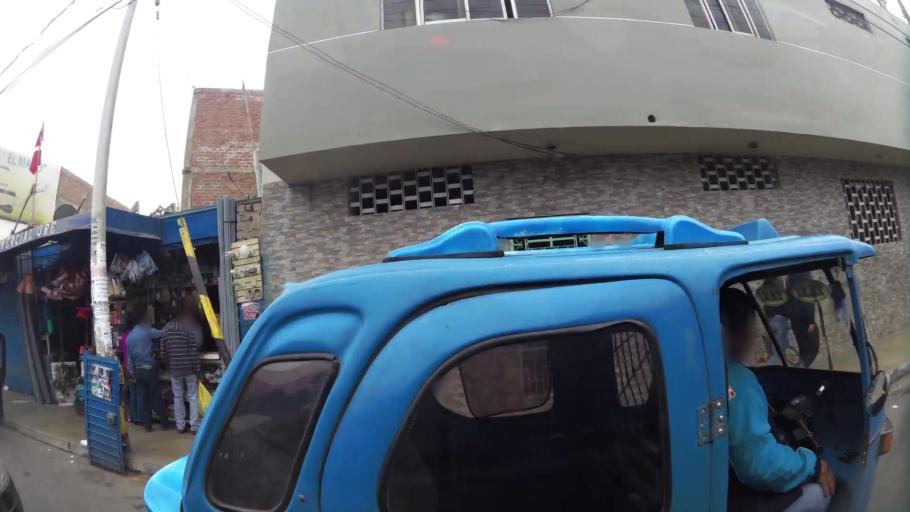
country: PE
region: Ica
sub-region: Provincia de Pisco
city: Pisco
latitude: -13.7126
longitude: -76.2051
